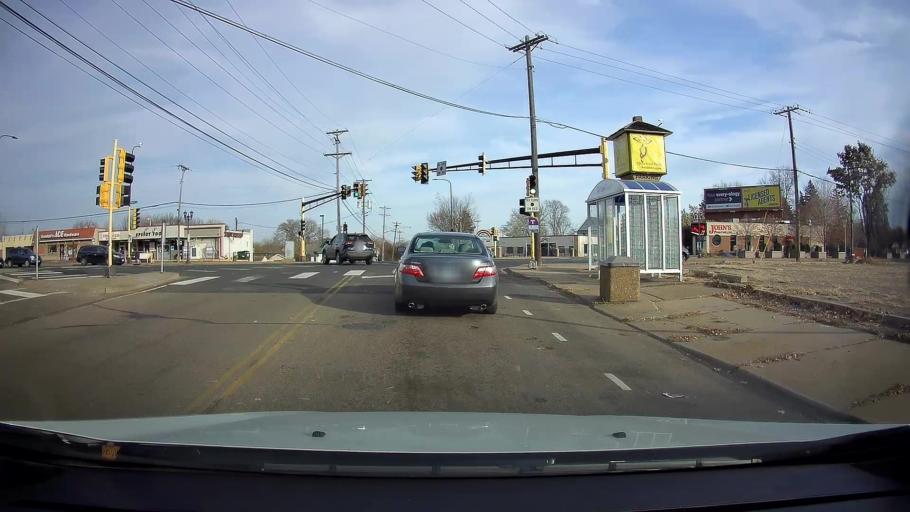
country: US
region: Minnesota
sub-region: Ramsey County
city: Saint Paul
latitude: 44.9702
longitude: -93.1268
